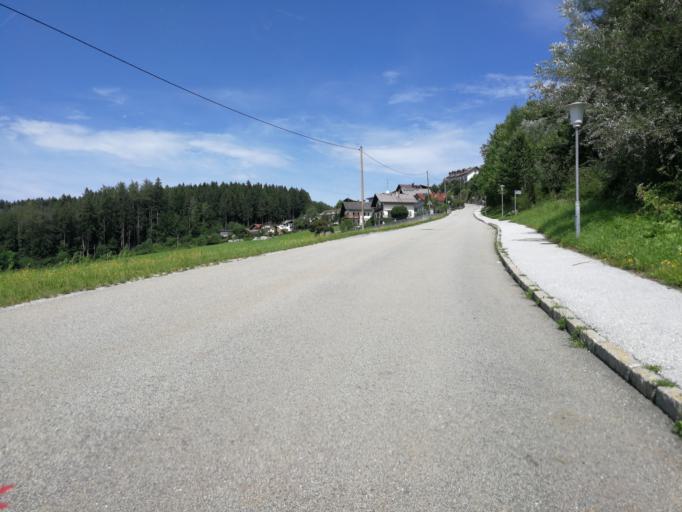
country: AT
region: Salzburg
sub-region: Politischer Bezirk Salzburg-Umgebung
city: Hallwang
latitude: 47.8395
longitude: 13.0657
